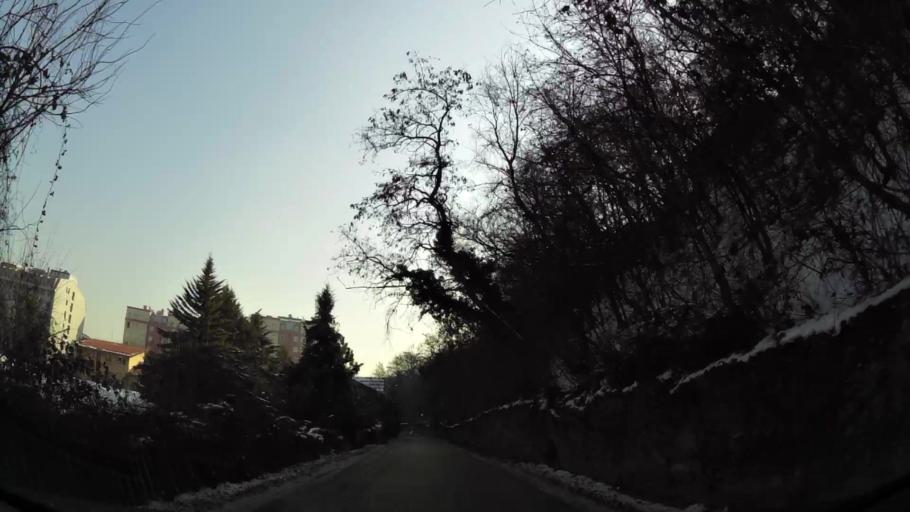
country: MK
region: Karpos
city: Skopje
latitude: 41.9870
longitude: 21.4254
